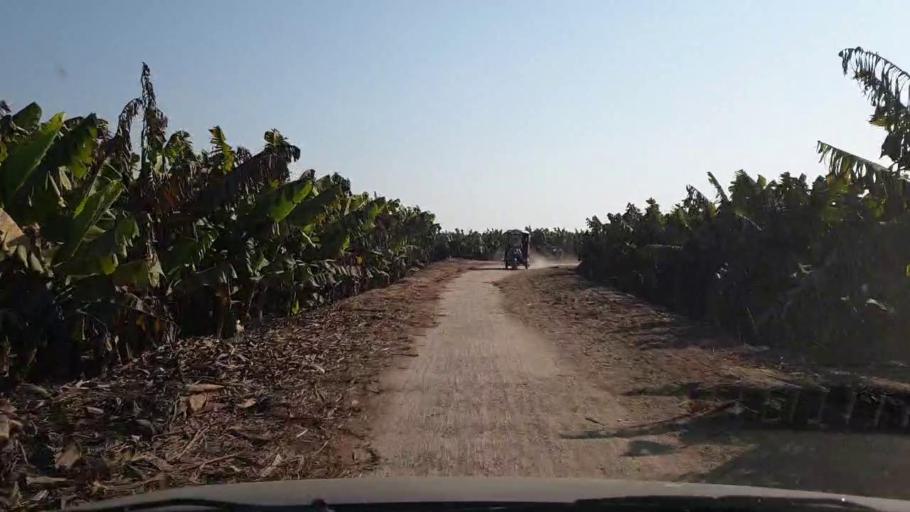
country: PK
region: Sindh
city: Tando Jam
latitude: 25.4359
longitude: 68.6132
